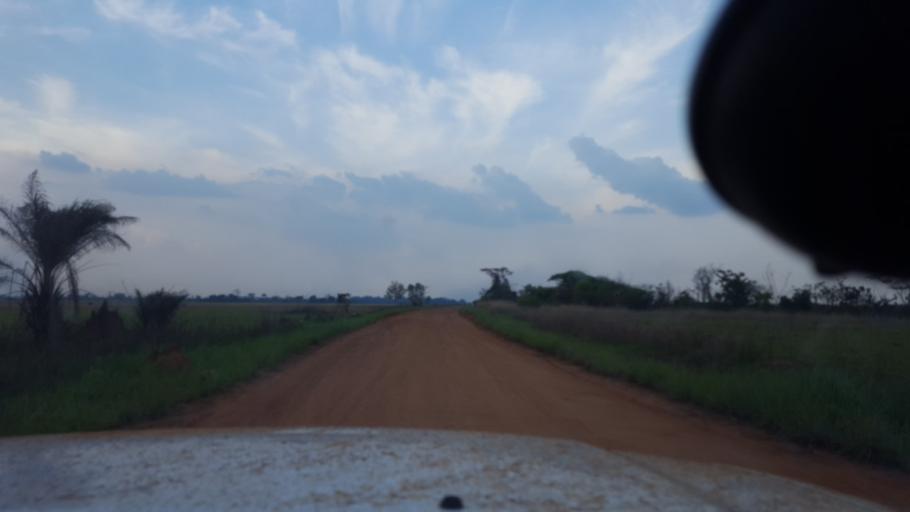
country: CD
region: Bandundu
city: Bandundu
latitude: -3.3867
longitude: 17.2591
